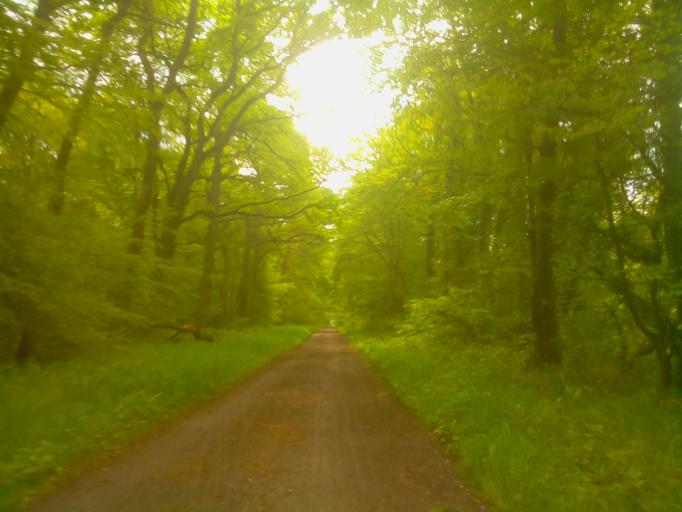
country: DE
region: Baden-Wuerttemberg
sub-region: Karlsruhe Region
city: Plankstadt
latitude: 49.4207
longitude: 8.5707
